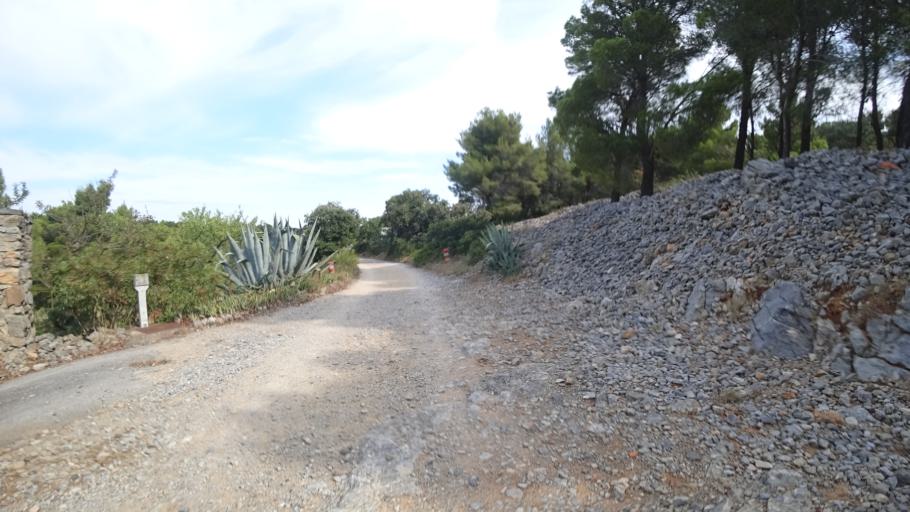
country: FR
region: Languedoc-Roussillon
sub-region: Departement de l'Aude
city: Leucate
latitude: 42.9009
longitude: 3.0325
